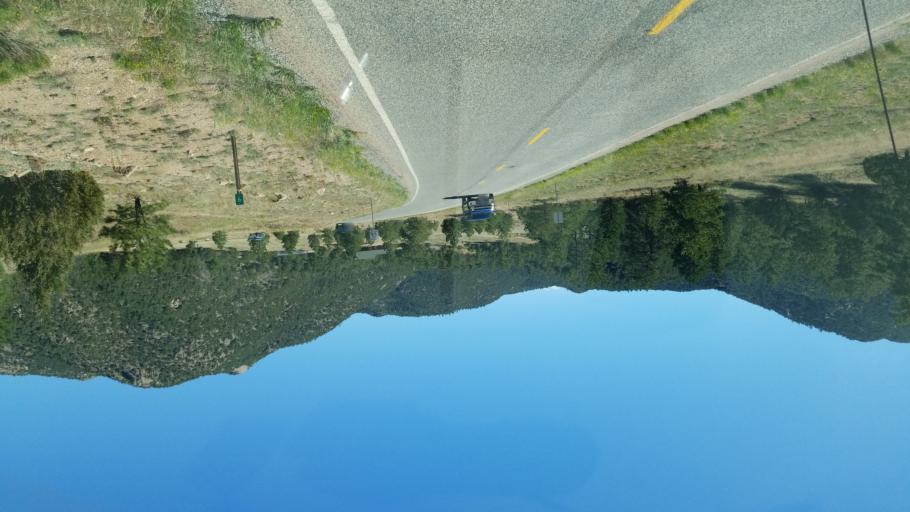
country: US
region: Colorado
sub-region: Fremont County
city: Canon City
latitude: 38.3822
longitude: -105.4560
